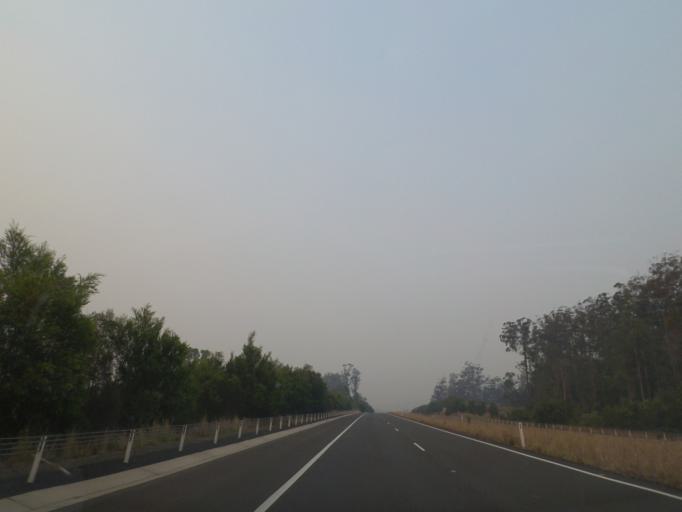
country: AU
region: New South Wales
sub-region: Nambucca Shire
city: Macksville
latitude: -30.7753
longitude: 152.8962
